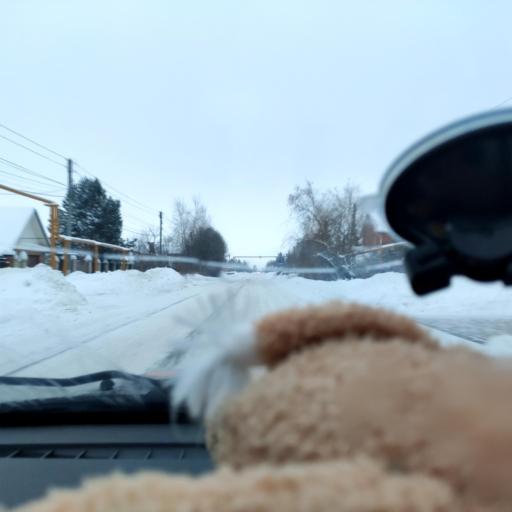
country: RU
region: Samara
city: Podstepki
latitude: 53.5193
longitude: 49.1807
